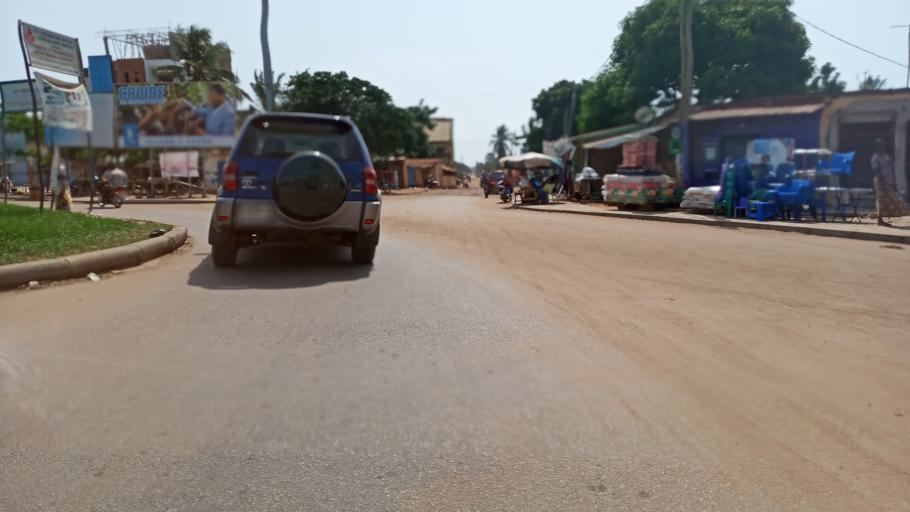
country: TG
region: Maritime
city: Lome
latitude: 6.2208
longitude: 1.2060
